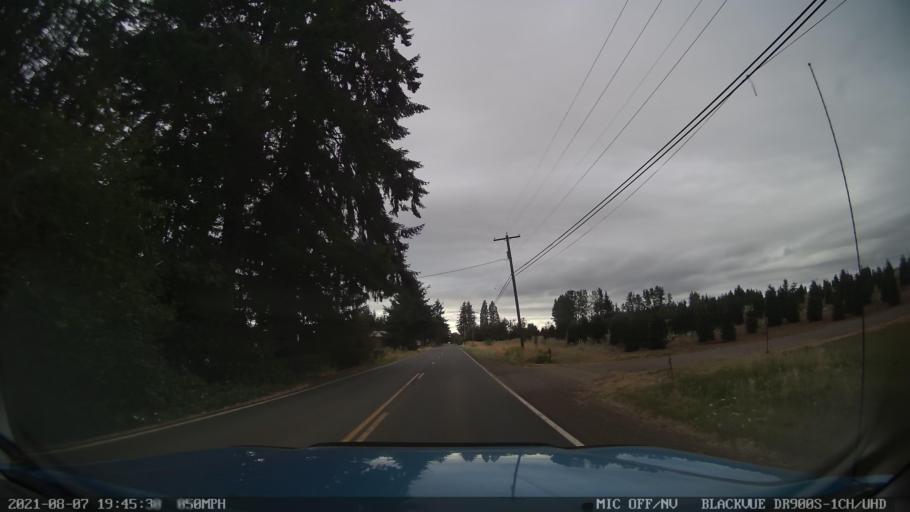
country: US
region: Oregon
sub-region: Marion County
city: Silverton
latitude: 44.9487
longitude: -122.6961
